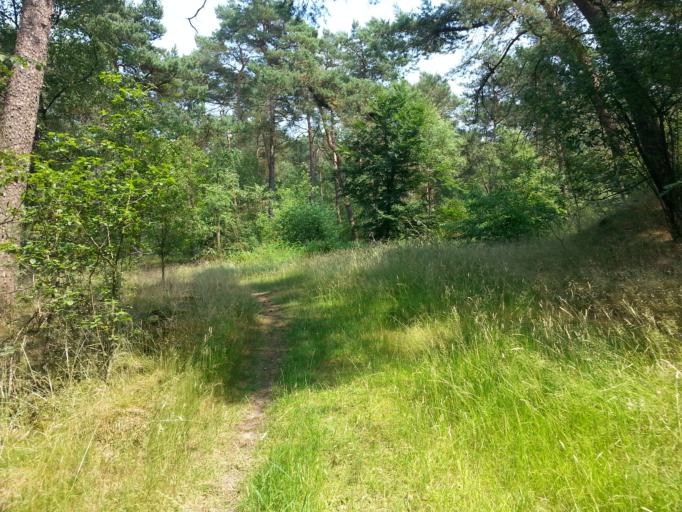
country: NL
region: Utrecht
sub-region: Gemeente Utrechtse Heuvelrug
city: Maarn
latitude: 52.1034
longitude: 5.3779
